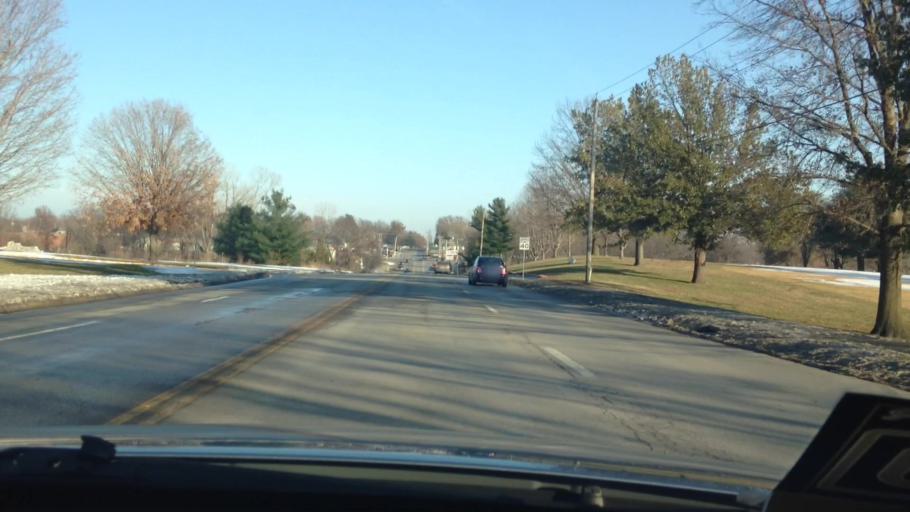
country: US
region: Kansas
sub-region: Leavenworth County
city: Lansing
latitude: 39.2669
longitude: -94.9052
